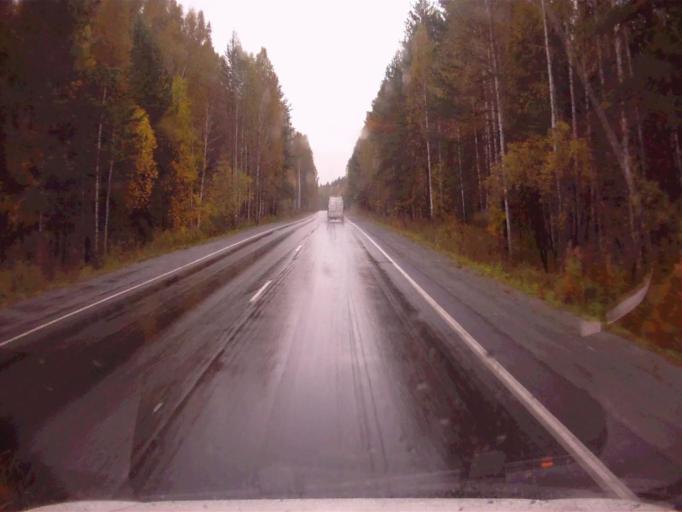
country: RU
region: Chelyabinsk
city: Tayginka
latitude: 55.5643
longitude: 60.6492
